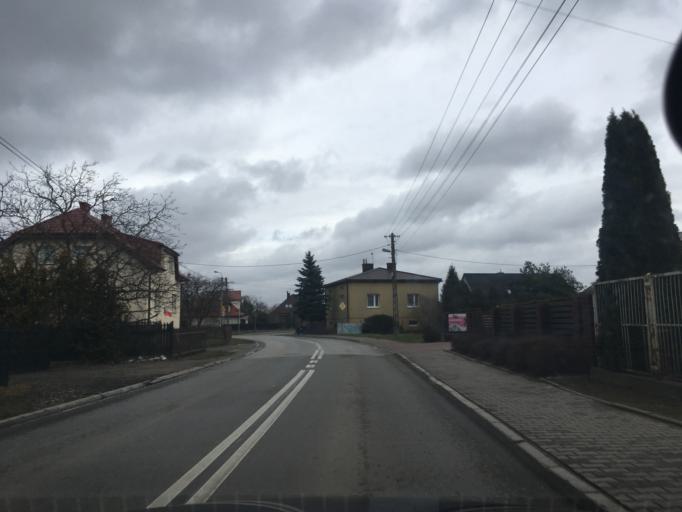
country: PL
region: Masovian Voivodeship
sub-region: Powiat pruszkowski
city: Rybie
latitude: 52.1259
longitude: 20.9579
